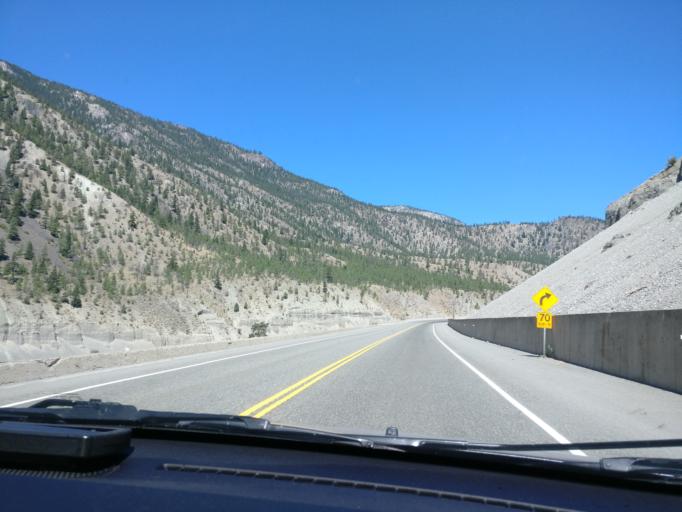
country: CA
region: British Columbia
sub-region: Thompson-Nicola Regional District
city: Ashcroft
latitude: 50.2779
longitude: -121.4056
